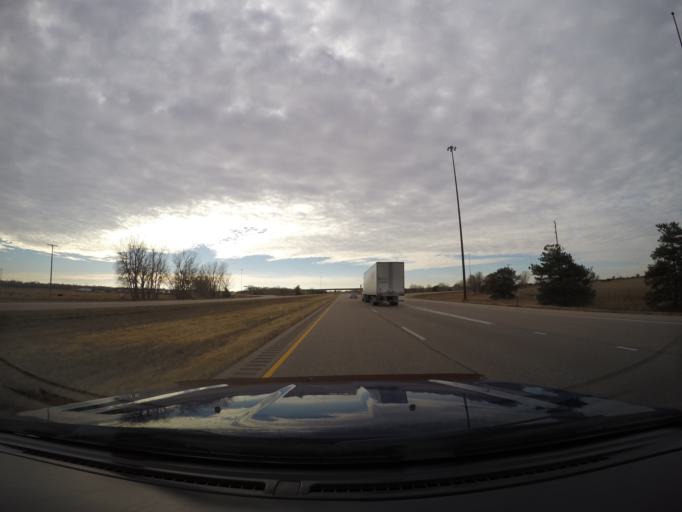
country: US
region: Nebraska
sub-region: Hall County
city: Wood River
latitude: 40.7641
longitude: -98.5838
